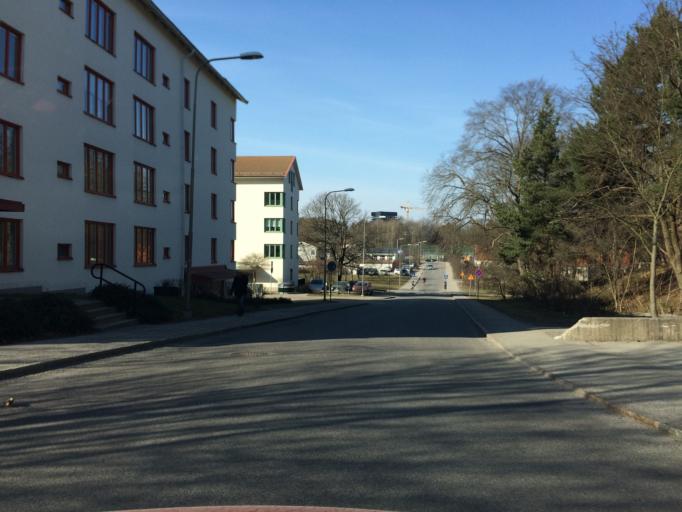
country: SE
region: Stockholm
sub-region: Stockholms Kommun
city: Arsta
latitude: 59.3004
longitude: 18.0409
